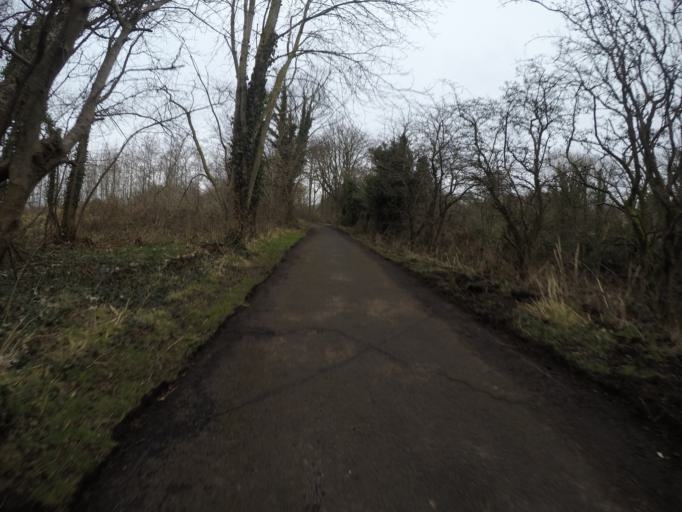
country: GB
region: Scotland
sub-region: North Ayrshire
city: Kilwinning
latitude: 55.6417
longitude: -4.6873
